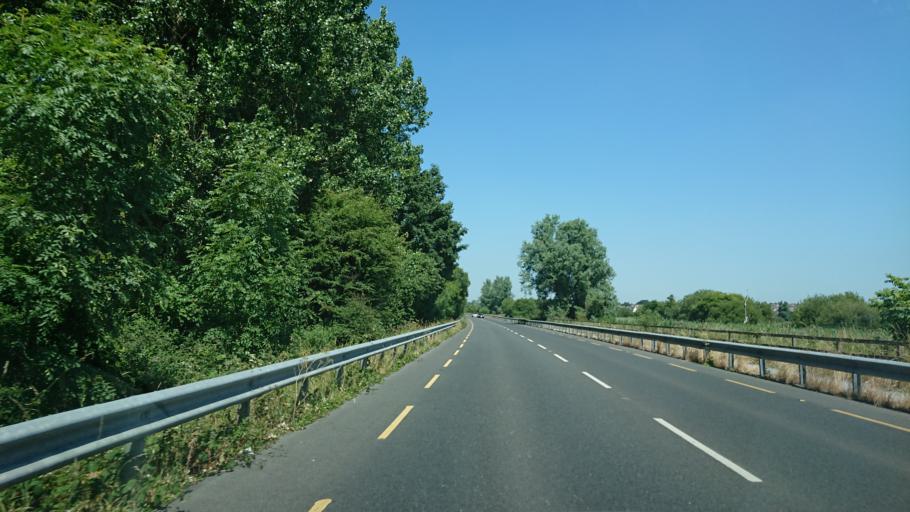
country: IE
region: Munster
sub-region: Waterford
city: Waterford
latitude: 52.2286
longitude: -7.1234
